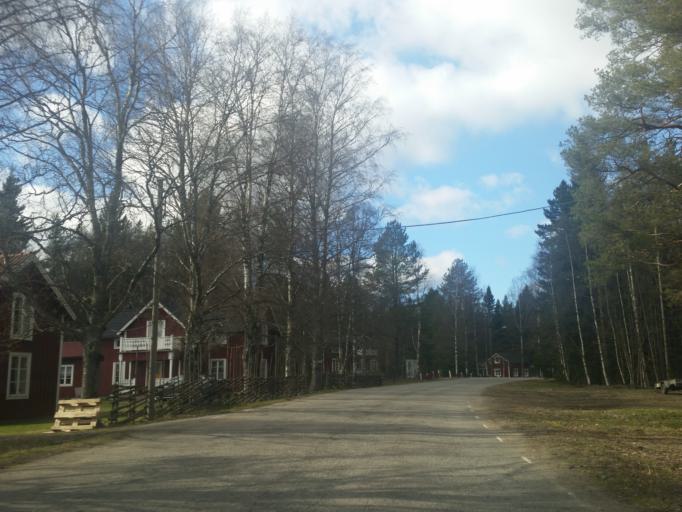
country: SE
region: Vaesterbotten
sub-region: Robertsfors Kommun
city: Robertsfors
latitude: 64.0485
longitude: 20.8506
